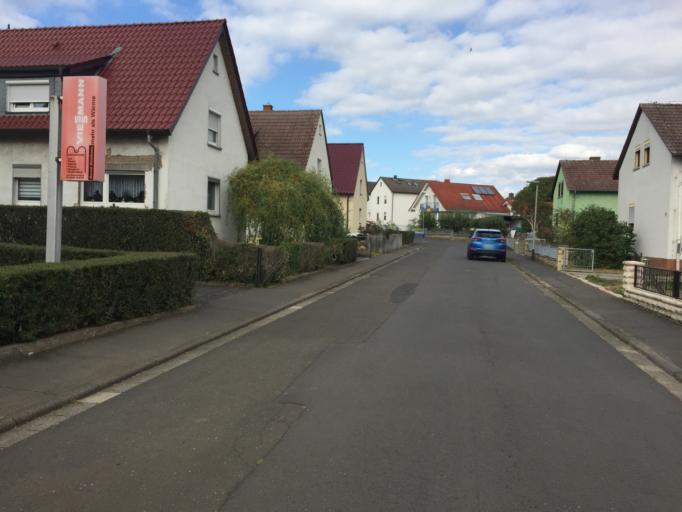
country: DE
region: Hesse
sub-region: Regierungsbezirk Darmstadt
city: Munzenberg
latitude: 50.4866
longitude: 8.7945
